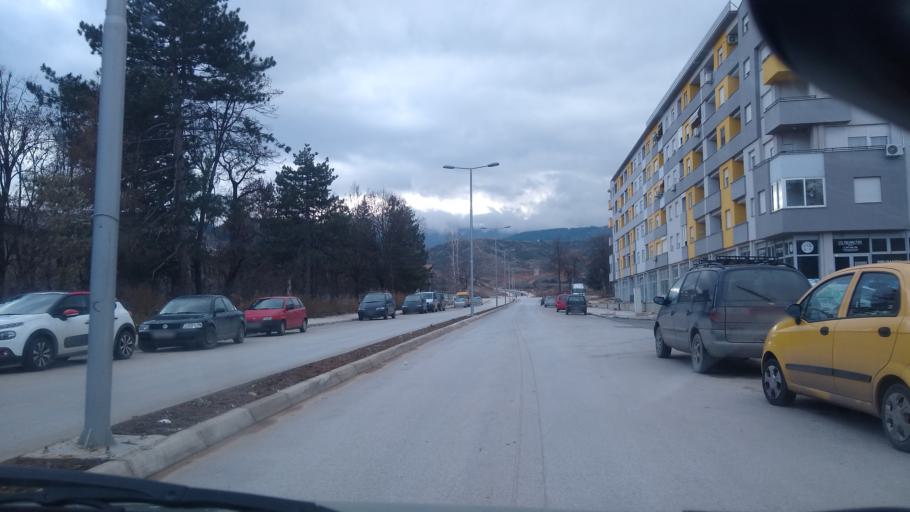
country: MK
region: Bitola
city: Bitola
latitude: 41.0227
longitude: 21.3286
